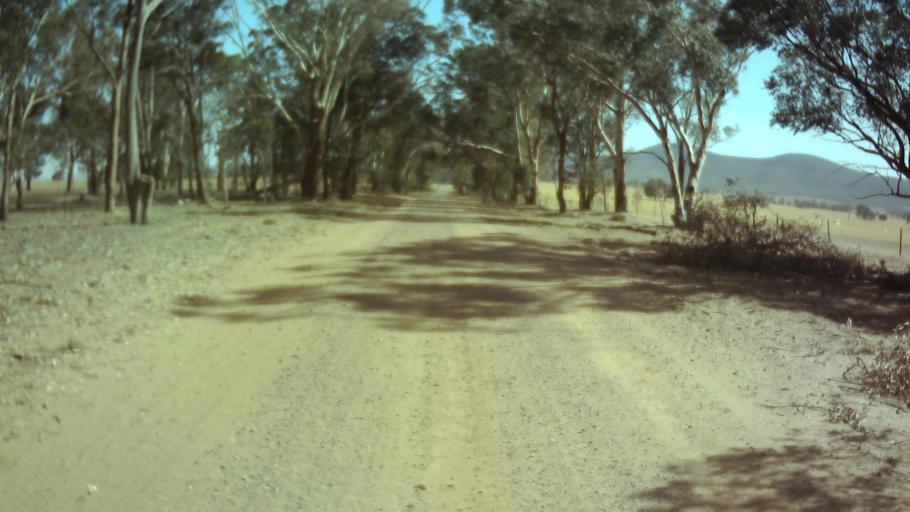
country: AU
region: New South Wales
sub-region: Weddin
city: Grenfell
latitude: -33.8484
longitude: 148.0168
